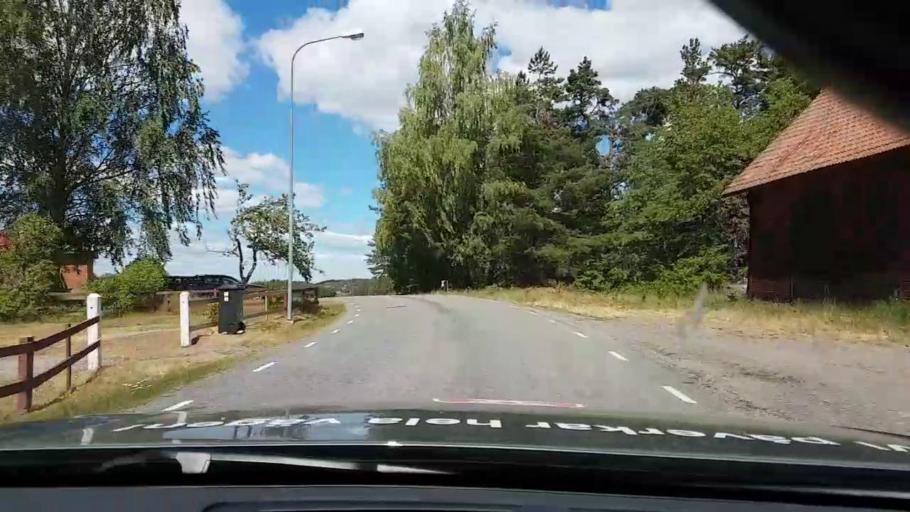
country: SE
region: Kalmar
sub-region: Vasterviks Kommun
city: Forserum
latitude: 58.0125
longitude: 16.5776
